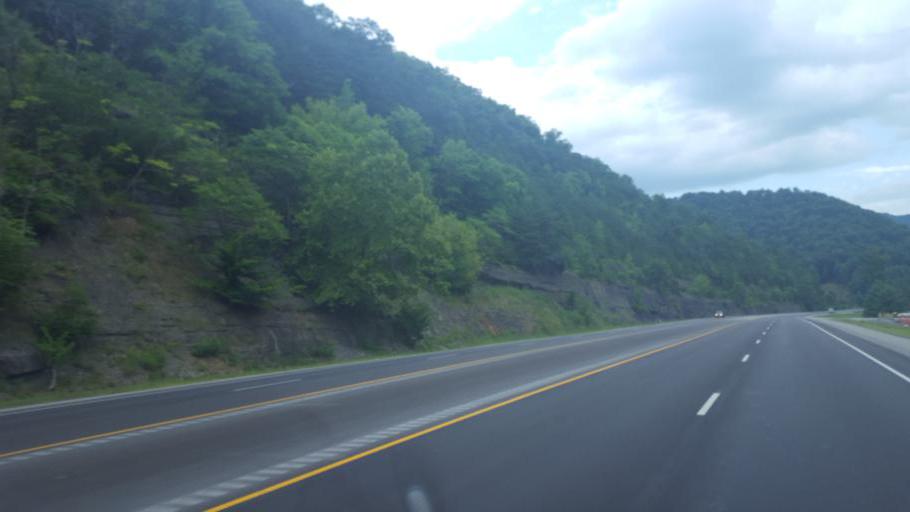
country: US
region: Kentucky
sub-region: Pike County
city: Pikeville
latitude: 37.3209
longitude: -82.5529
